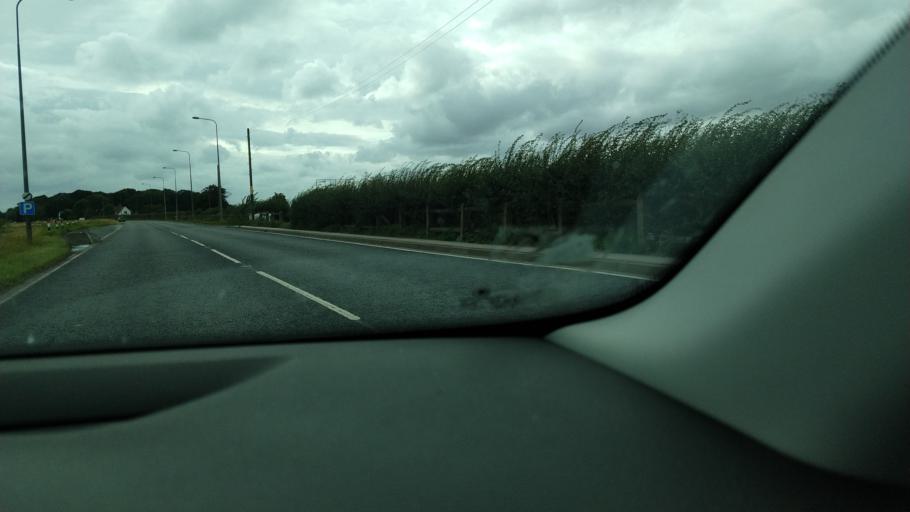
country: GB
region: England
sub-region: East Riding of Yorkshire
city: Airmyn
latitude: 53.7070
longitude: -0.9223
